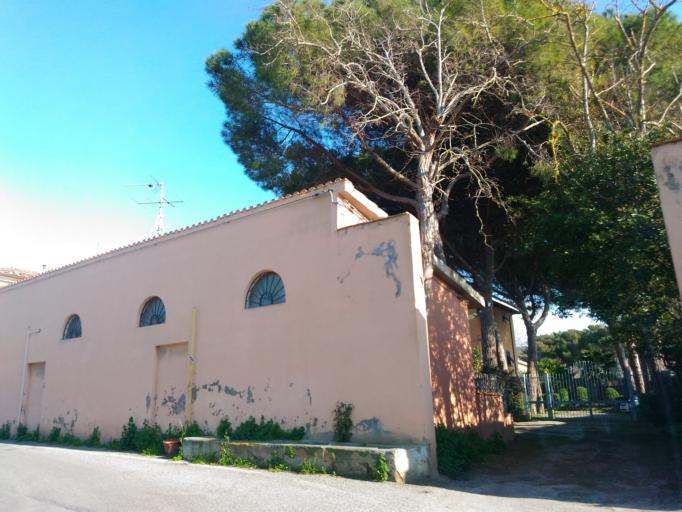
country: IT
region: Tuscany
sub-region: Provincia di Livorno
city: Livorno
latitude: 43.5091
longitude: 10.3417
